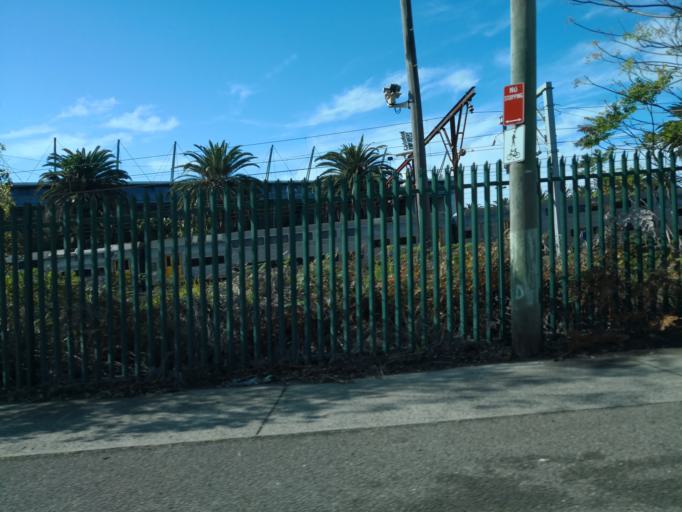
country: AU
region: New South Wales
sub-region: Gosford Shire
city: Gosford
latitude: -33.4278
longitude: 151.3365
